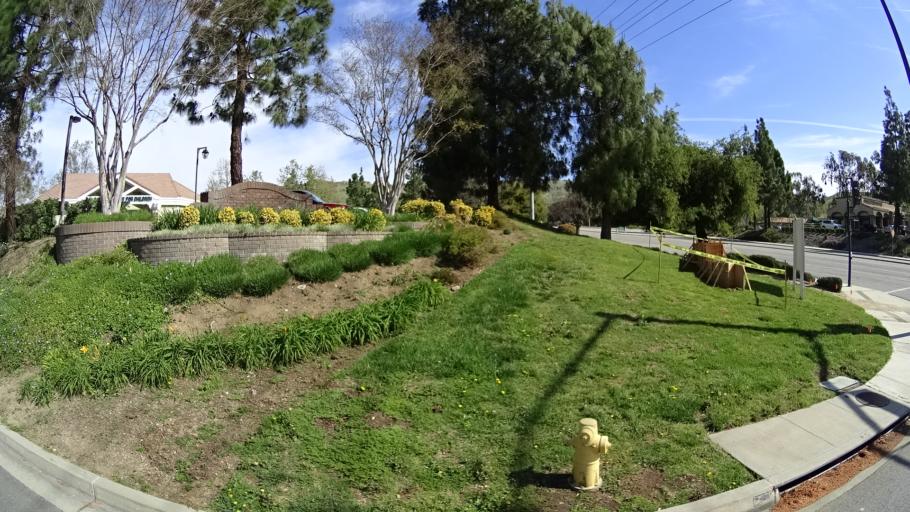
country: US
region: California
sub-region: Ventura County
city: Oak Park
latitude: 34.1831
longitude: -118.7867
